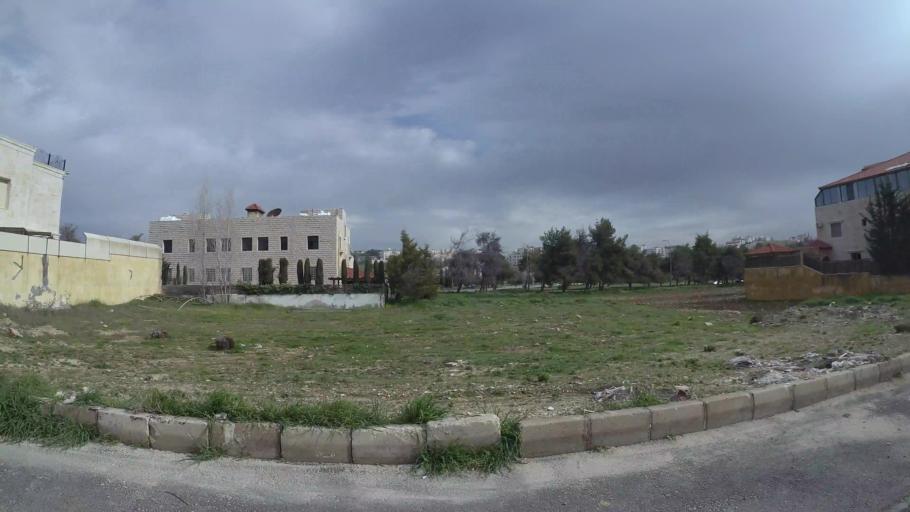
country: JO
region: Amman
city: Wadi as Sir
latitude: 31.9917
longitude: 35.8261
